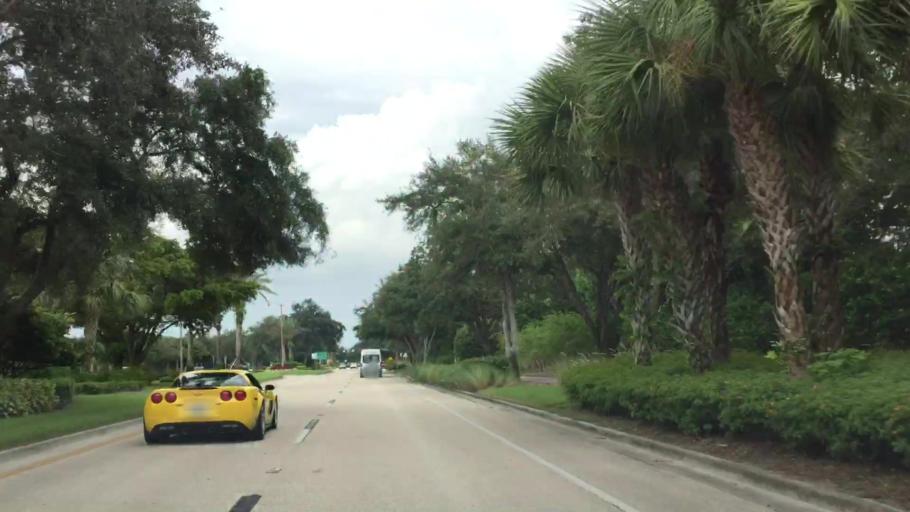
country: US
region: Florida
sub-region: Lee County
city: Estero
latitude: 26.3960
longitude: -81.7876
